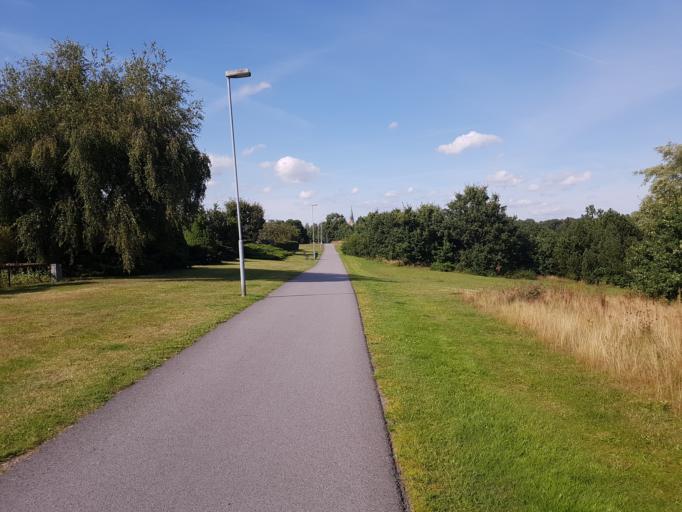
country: SE
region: Skane
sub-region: Sjobo Kommun
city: Sjoebo
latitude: 55.6394
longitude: 13.6998
